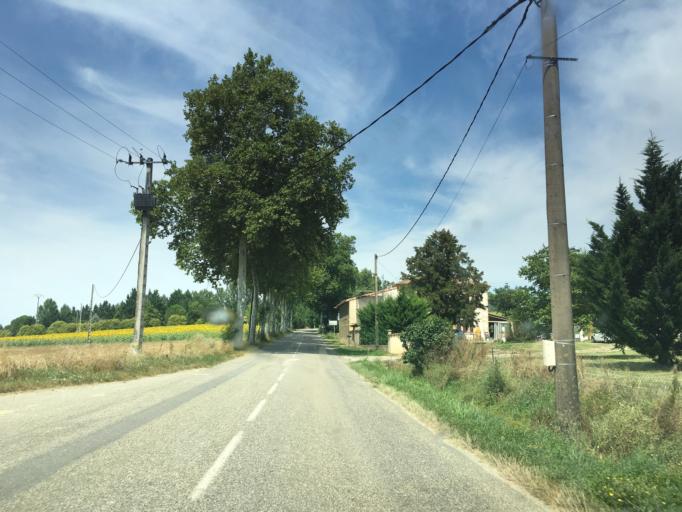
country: FR
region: Midi-Pyrenees
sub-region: Departement du Gers
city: Fleurance
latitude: 43.8522
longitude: 0.6772
